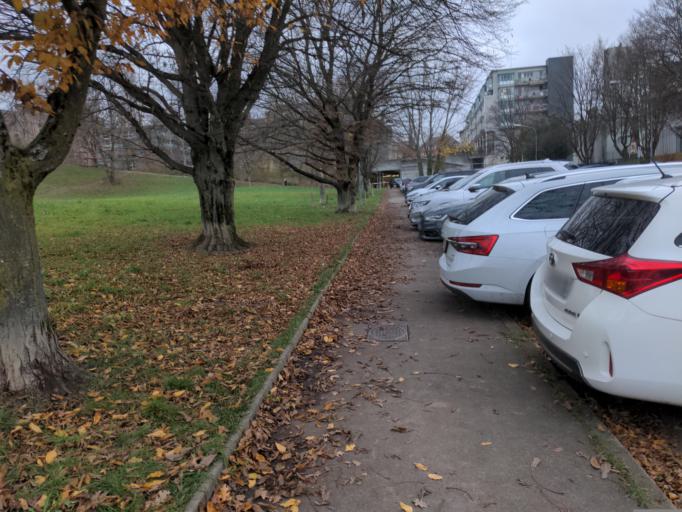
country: CH
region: Zurich
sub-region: Bezirk Zuerich
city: Zuerich (Kreis 3) / Alt-Wiedikon
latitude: 47.3561
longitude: 8.5198
